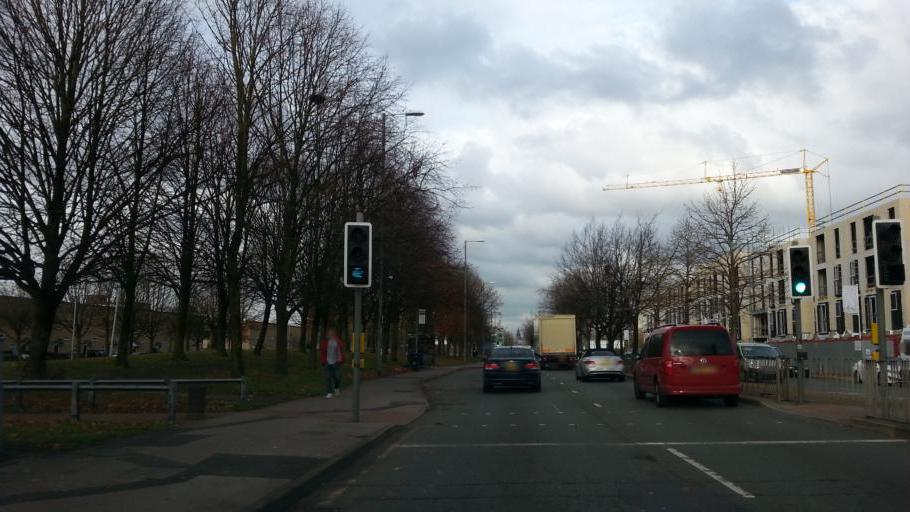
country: GB
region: England
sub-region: Manchester
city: Hulme
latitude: 53.4564
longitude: -2.2452
